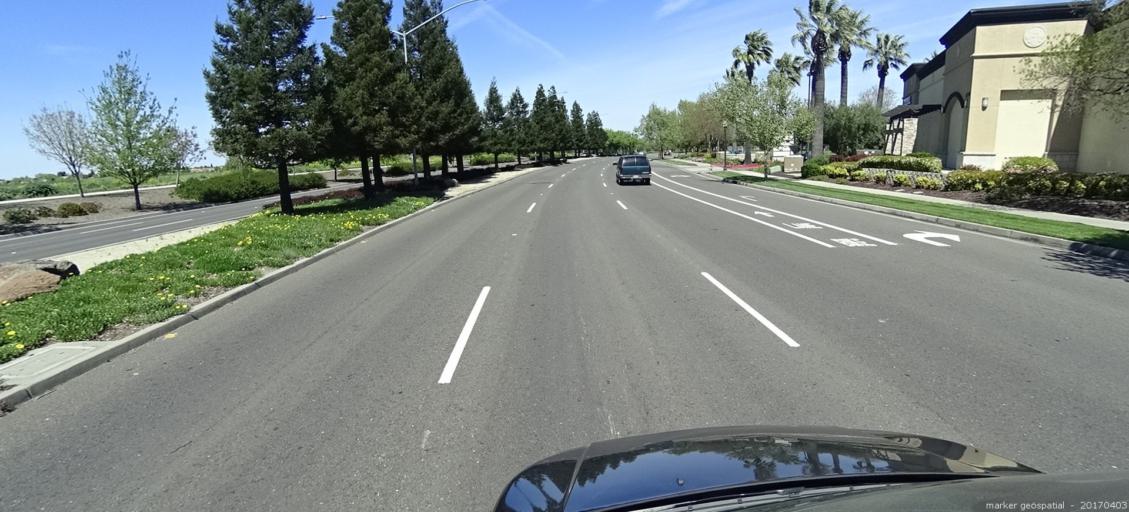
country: US
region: California
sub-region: Sacramento County
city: Rio Linda
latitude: 38.6597
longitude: -121.5120
